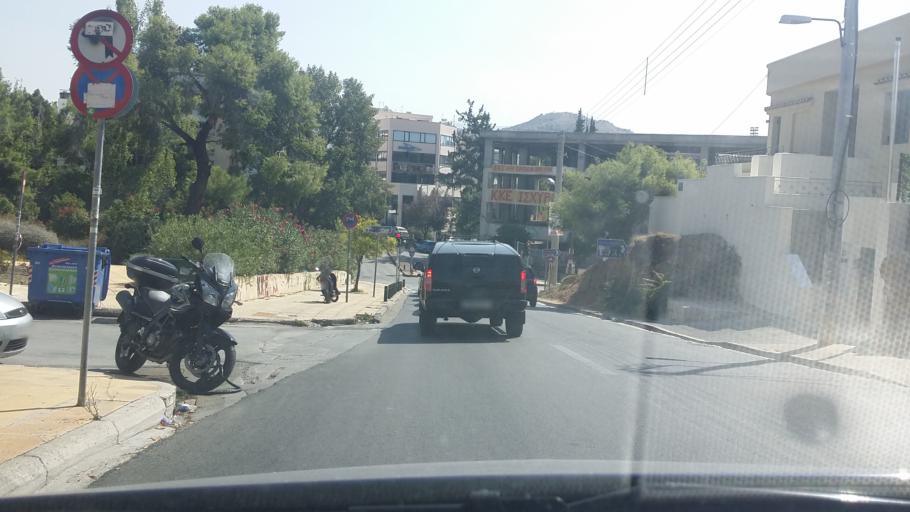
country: GR
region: Attica
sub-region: Nomarchia Athinas
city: Nea Ionia
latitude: 38.0405
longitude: 23.7613
